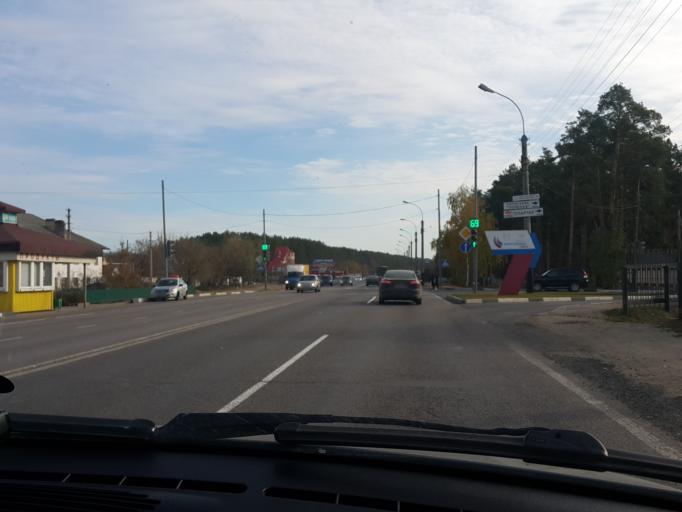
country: RU
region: Tambov
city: Donskoye
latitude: 52.7156
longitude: 41.5088
